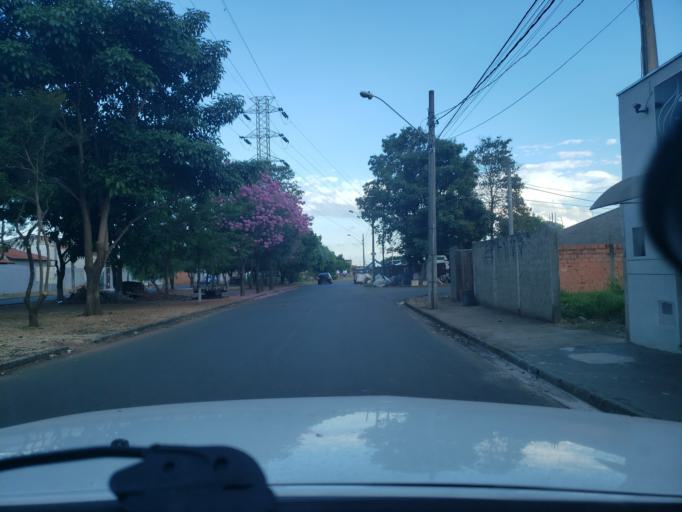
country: BR
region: Sao Paulo
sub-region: Moji-Guacu
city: Mogi-Gaucu
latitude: -22.3268
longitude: -46.9213
